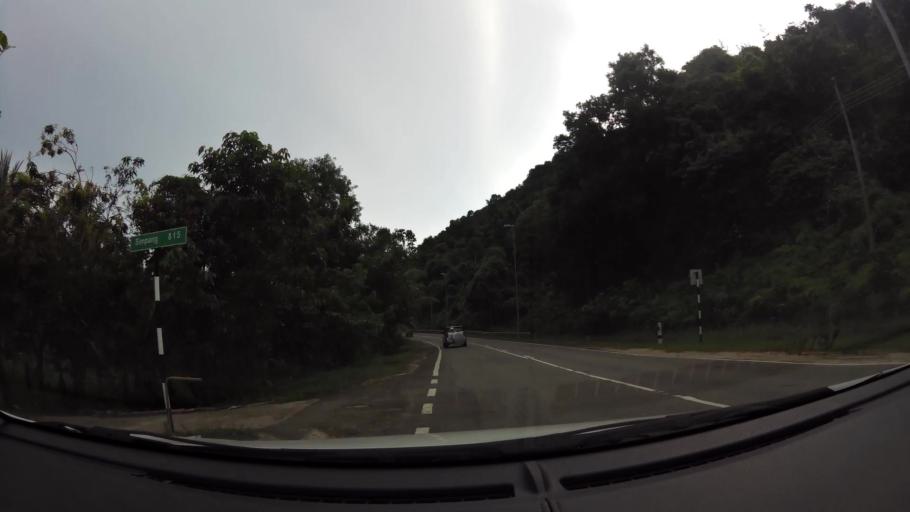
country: BN
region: Brunei and Muara
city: Bandar Seri Begawan
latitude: 4.9219
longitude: 115.0098
